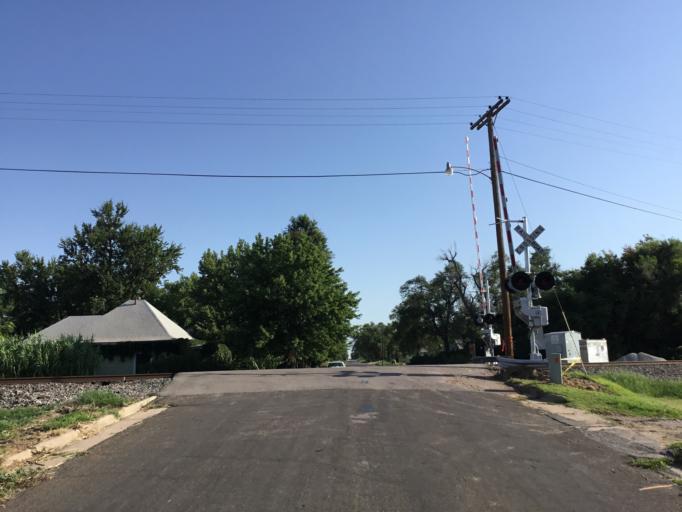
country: US
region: Kansas
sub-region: Pratt County
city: Pratt
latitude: 37.6468
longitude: -98.7485
